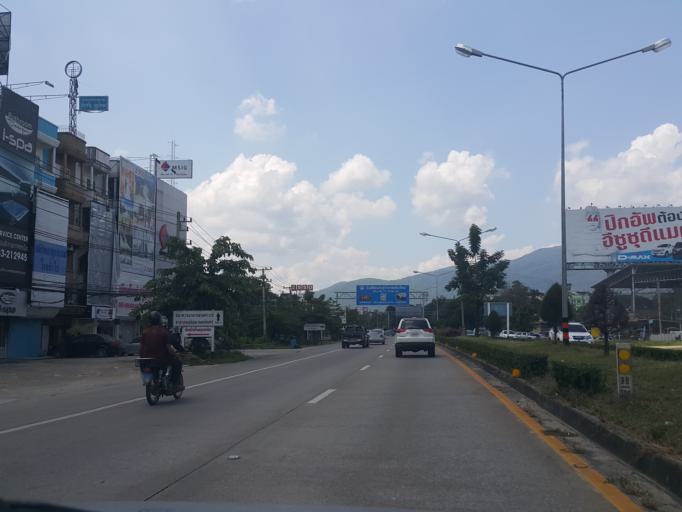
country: TH
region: Chiang Mai
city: Chiang Mai
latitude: 18.8102
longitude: 98.9766
